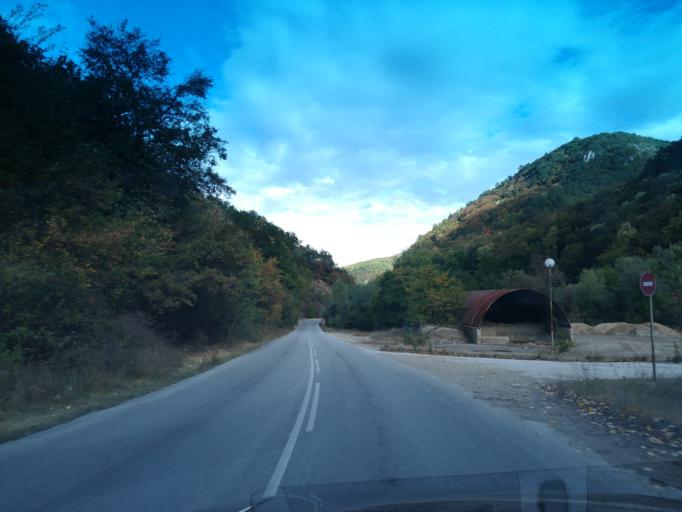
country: BG
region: Pazardzhik
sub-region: Obshtina Peshtera
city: Peshtera
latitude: 42.0156
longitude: 24.2640
